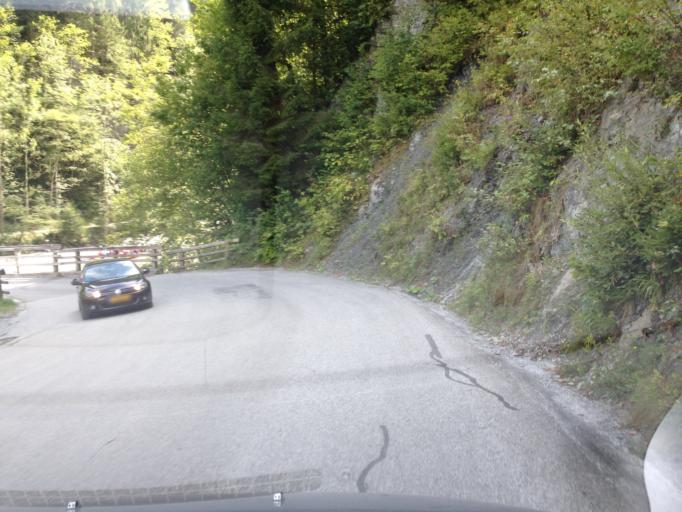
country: AT
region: Salzburg
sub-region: Politischer Bezirk Zell am See
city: Taxenbach
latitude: 47.2930
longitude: 12.9755
